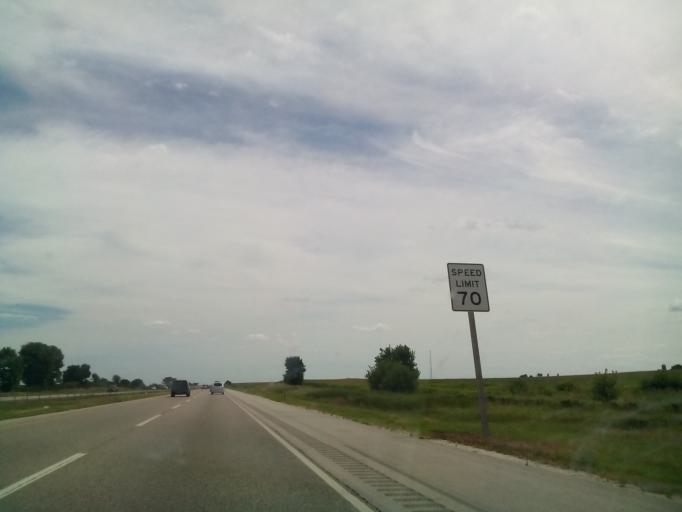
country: US
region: Illinois
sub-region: Kane County
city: Maple Park
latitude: 41.8944
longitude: -88.6393
